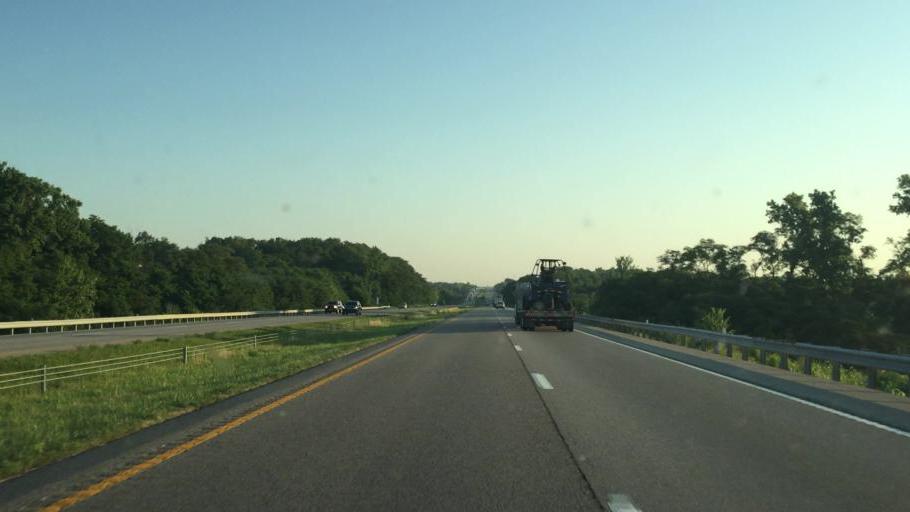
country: US
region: Missouri
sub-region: Platte County
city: Weston
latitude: 39.5621
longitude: -94.7881
